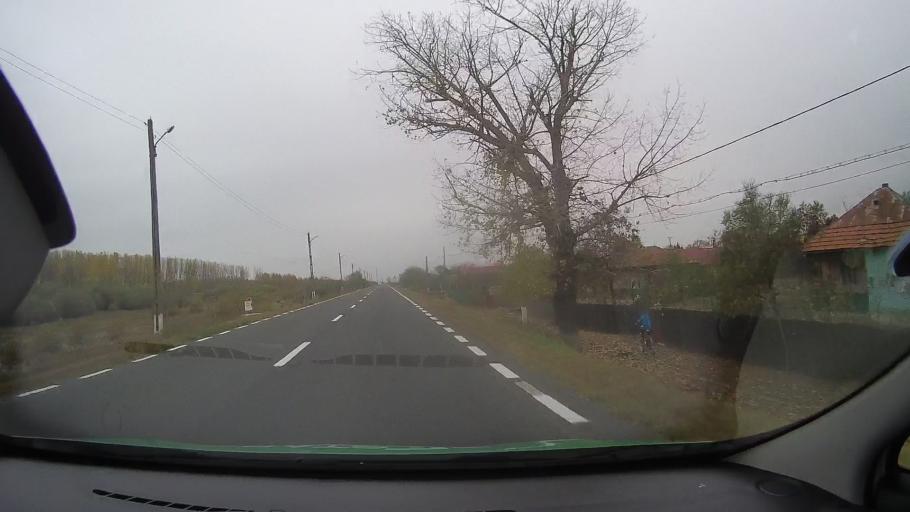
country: RO
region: Ialomita
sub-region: Comuna Giurgeni
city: Giurgeni
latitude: 44.7361
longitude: 27.8552
